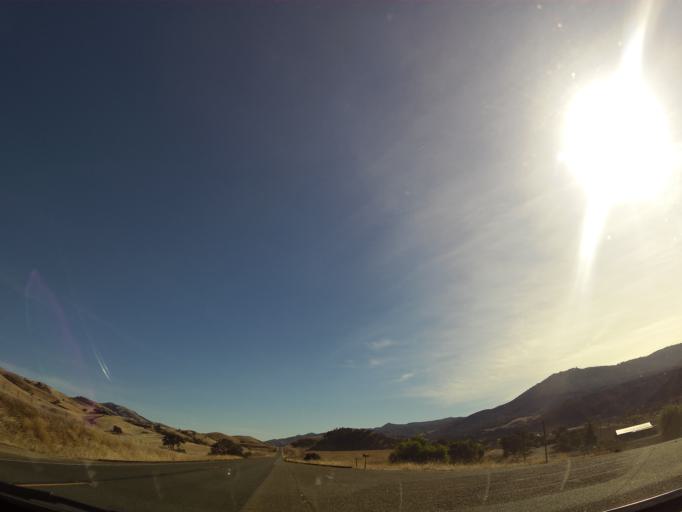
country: US
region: California
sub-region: San Benito County
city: Ridgemark
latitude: 36.6626
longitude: -121.2461
